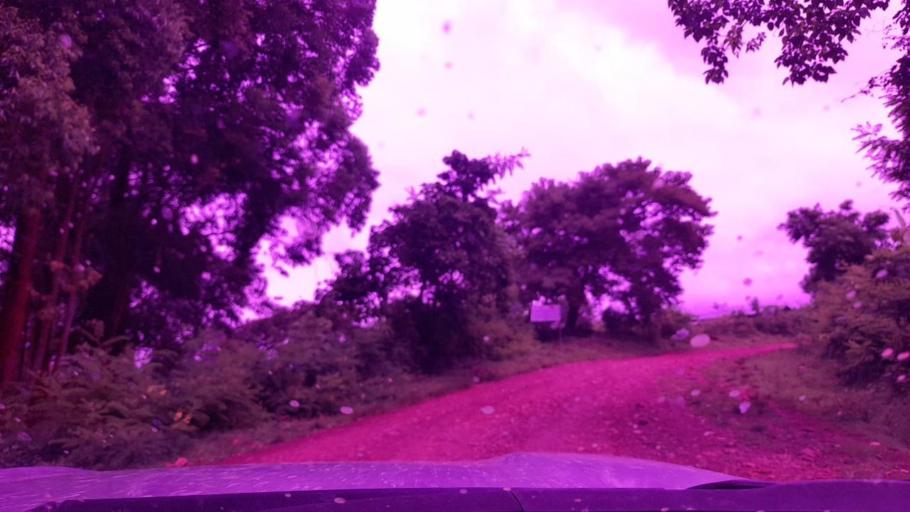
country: ET
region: Southern Nations, Nationalities, and People's Region
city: Bonga
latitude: 7.5464
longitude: 35.8496
